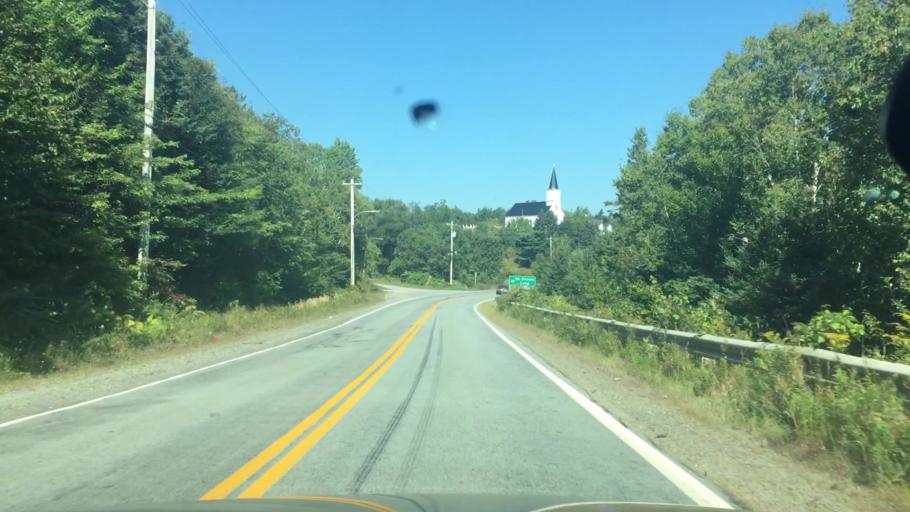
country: CA
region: Nova Scotia
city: New Glasgow
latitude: 44.9214
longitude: -62.5445
